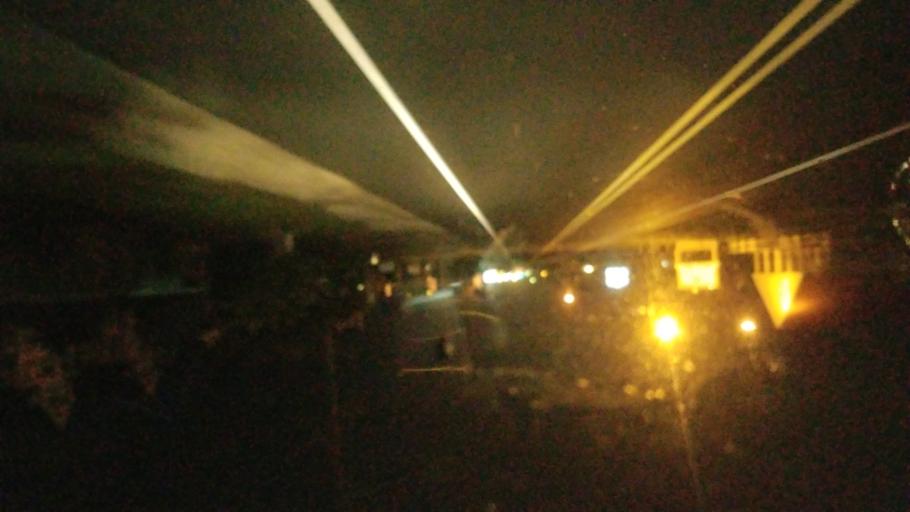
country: US
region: North Carolina
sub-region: Dare County
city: Kill Devil Hills
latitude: 36.0098
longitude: -75.6548
